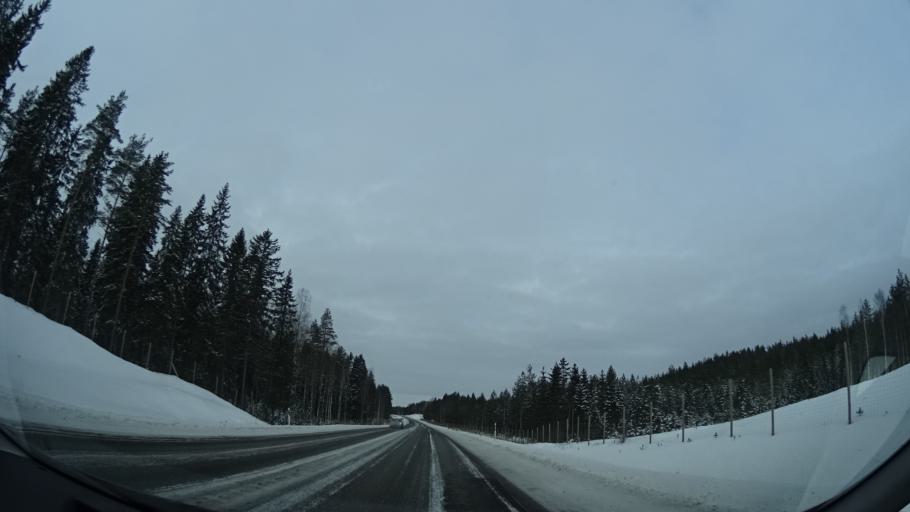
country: FI
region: Uusimaa
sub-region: Helsinki
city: Kaerkoelae
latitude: 60.6155
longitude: 24.0246
